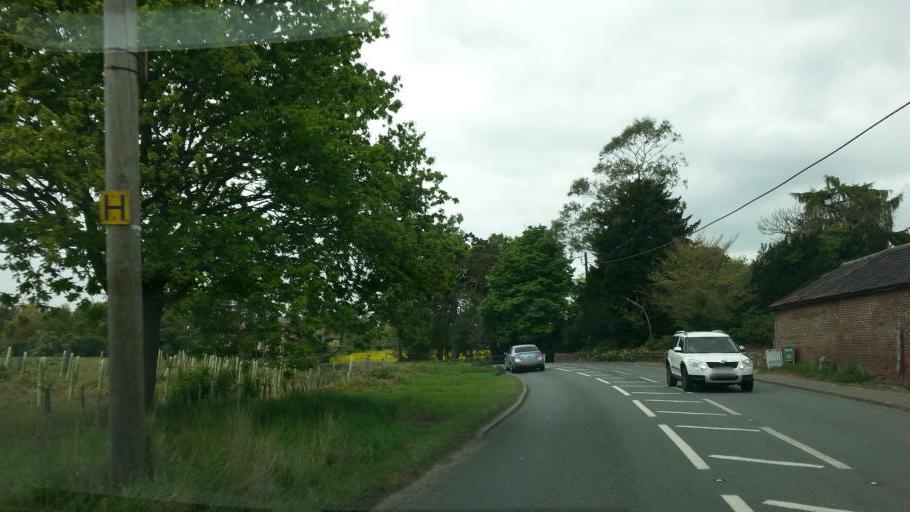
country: GB
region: England
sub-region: Suffolk
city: Capel Saint Mary
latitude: 52.0502
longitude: 1.0528
